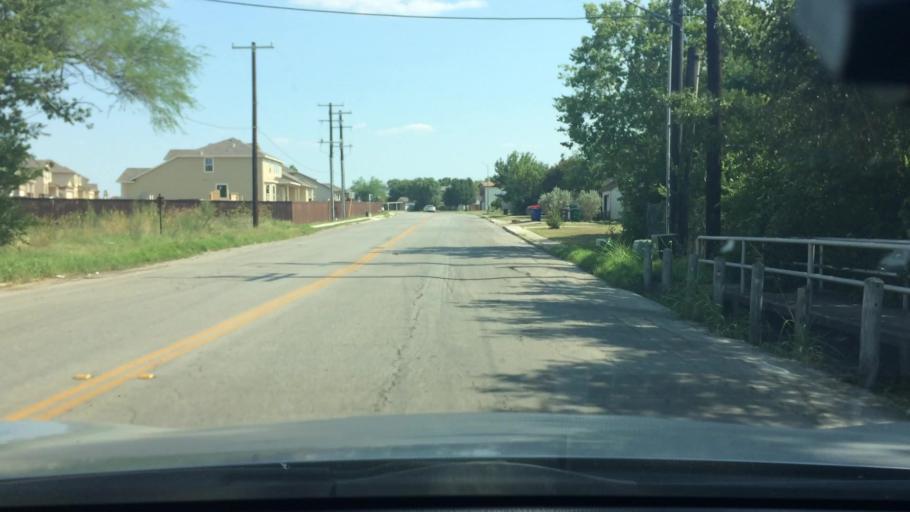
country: US
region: Texas
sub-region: Bexar County
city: Kirby
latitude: 29.4733
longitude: -98.3753
